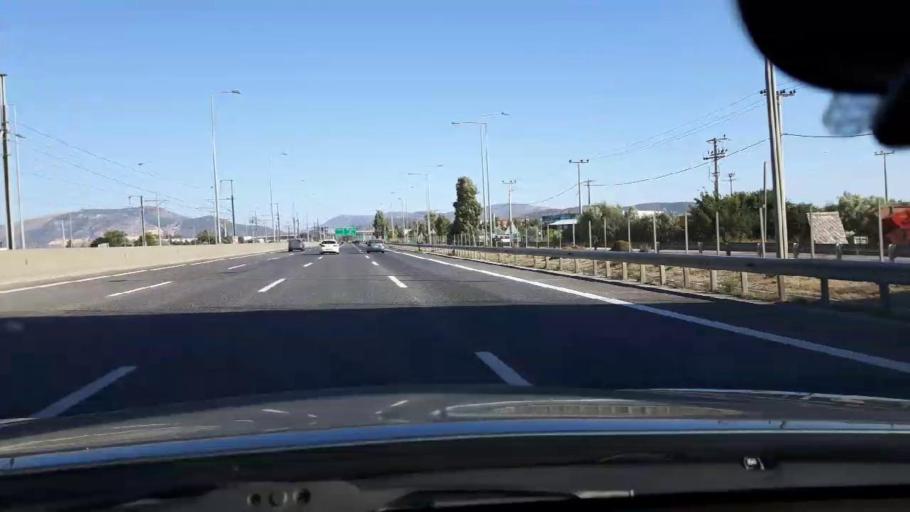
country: GR
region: Attica
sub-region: Nomarchia Anatolikis Attikis
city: Koropi
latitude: 37.9081
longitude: 23.8994
